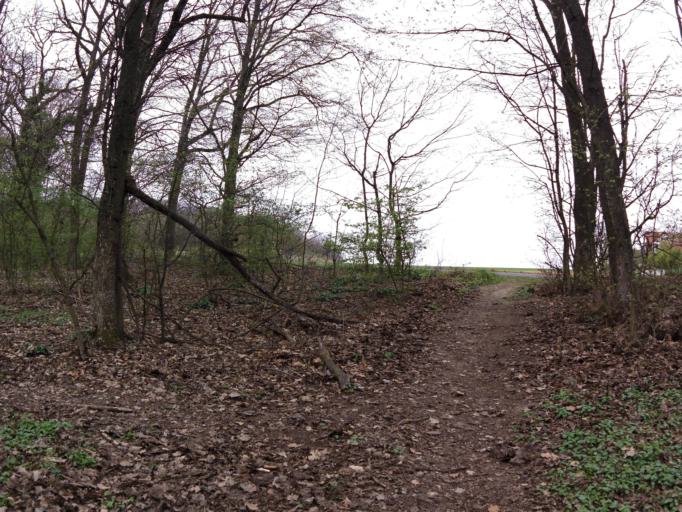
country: DE
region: Bavaria
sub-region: Regierungsbezirk Unterfranken
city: Rottendorf
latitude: 49.7985
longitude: 10.0207
